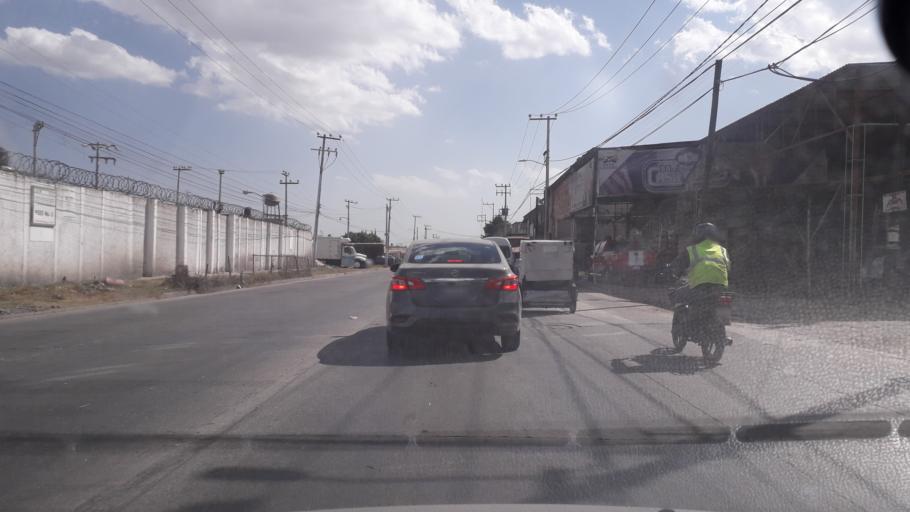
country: MX
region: Mexico
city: Ecatepec
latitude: 19.6288
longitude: -99.0511
